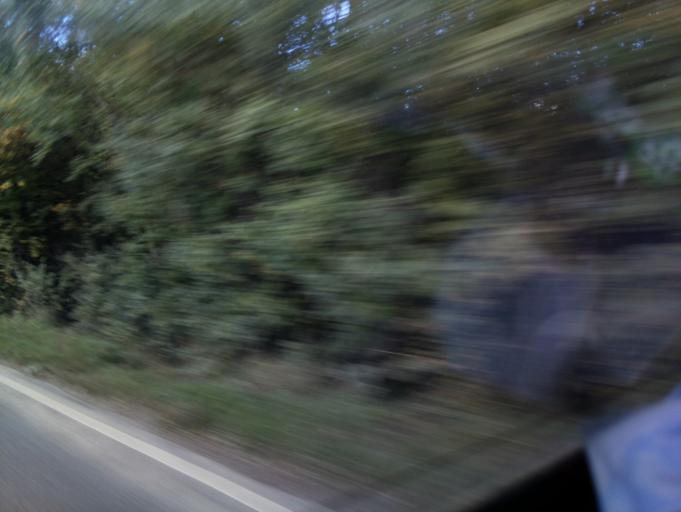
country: GB
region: England
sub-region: Herefordshire
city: Ocle Pychard
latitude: 52.0581
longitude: -2.5308
